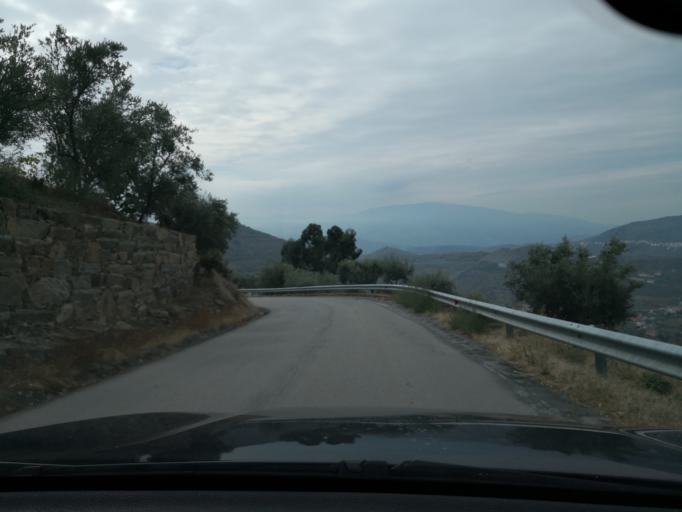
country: PT
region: Vila Real
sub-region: Peso da Regua
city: Peso da Regua
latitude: 41.1963
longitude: -7.7300
